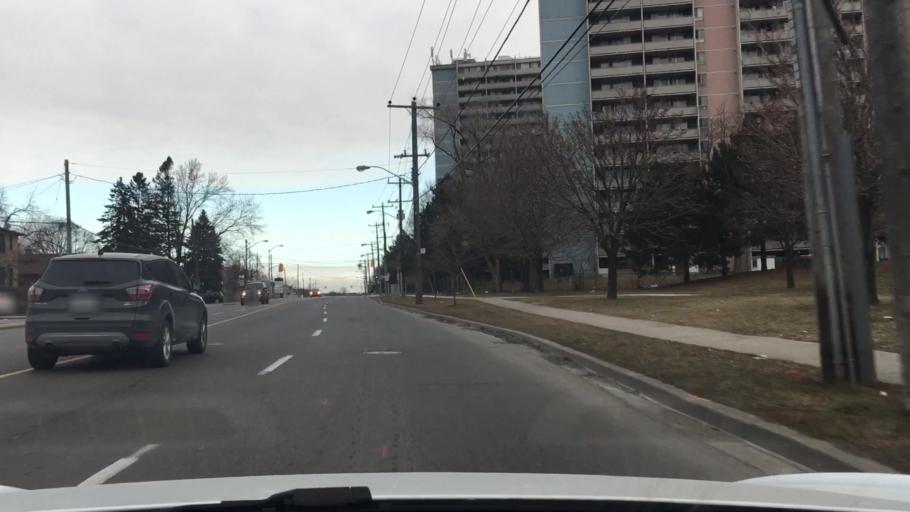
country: CA
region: Ontario
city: Scarborough
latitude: 43.7262
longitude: -79.2532
